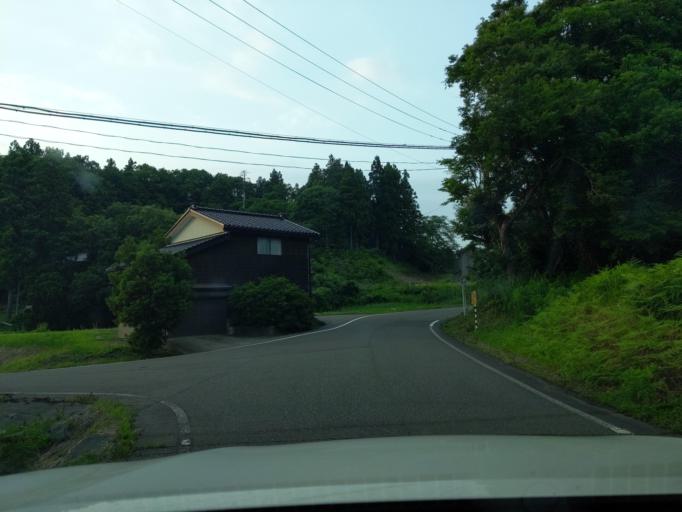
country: JP
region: Niigata
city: Kashiwazaki
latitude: 37.4404
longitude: 138.6537
